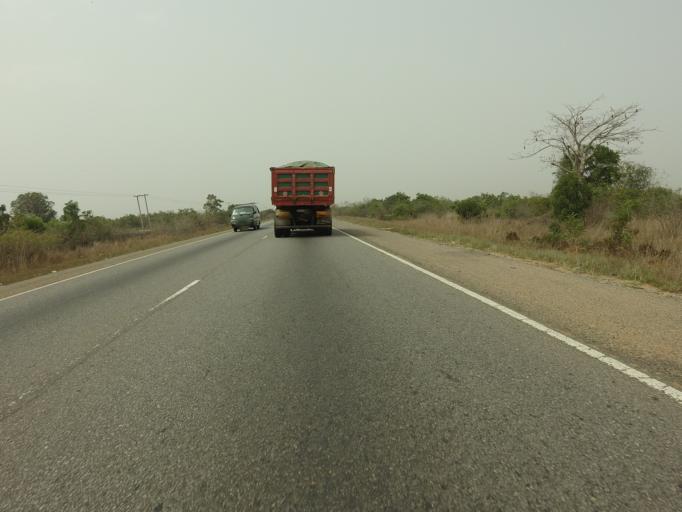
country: GH
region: Greater Accra
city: Tema
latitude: 5.8692
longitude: 0.3152
